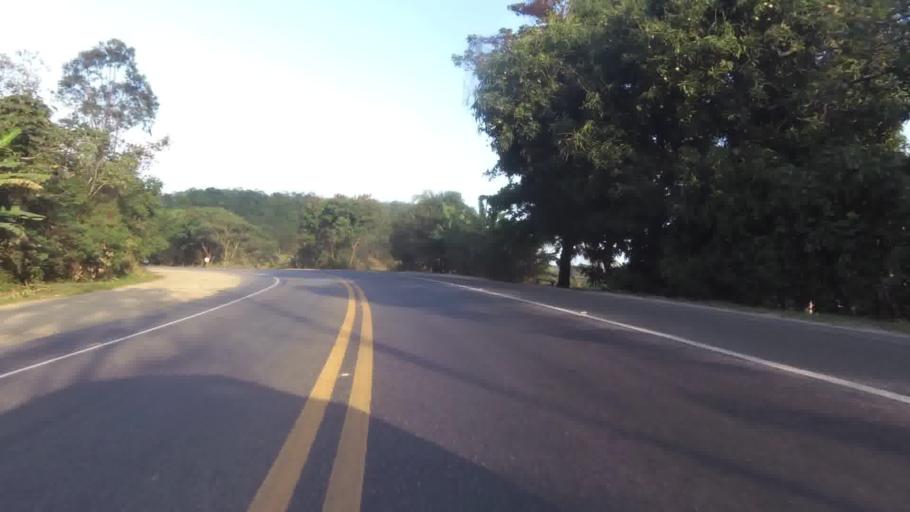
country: BR
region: Espirito Santo
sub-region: Rio Novo Do Sul
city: Rio Novo do Sul
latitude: -20.8665
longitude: -40.8959
